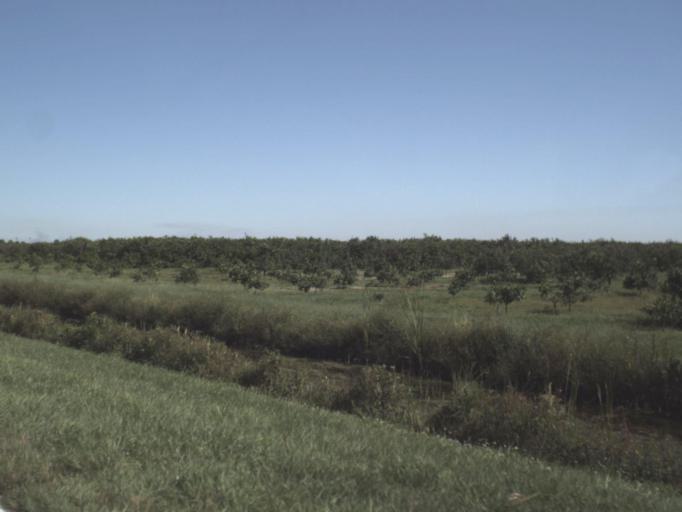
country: US
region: Florida
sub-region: Glades County
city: Moore Haven
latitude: 26.7683
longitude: -81.1912
